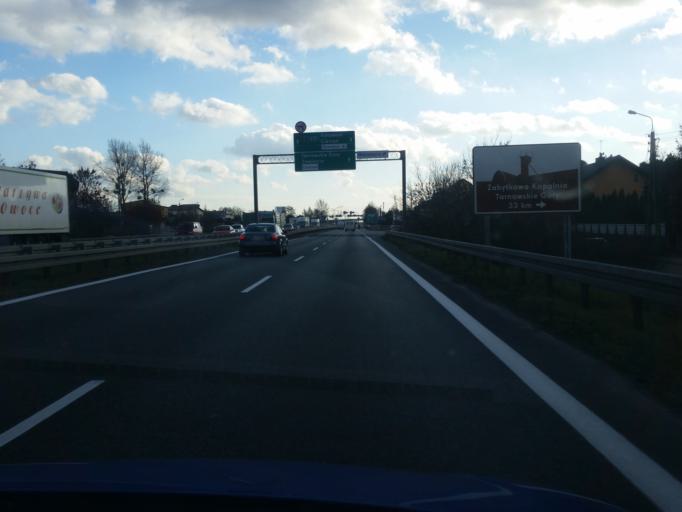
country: PL
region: Silesian Voivodeship
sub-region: Powiat bedzinski
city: Siewierz
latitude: 50.4694
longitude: 19.2293
